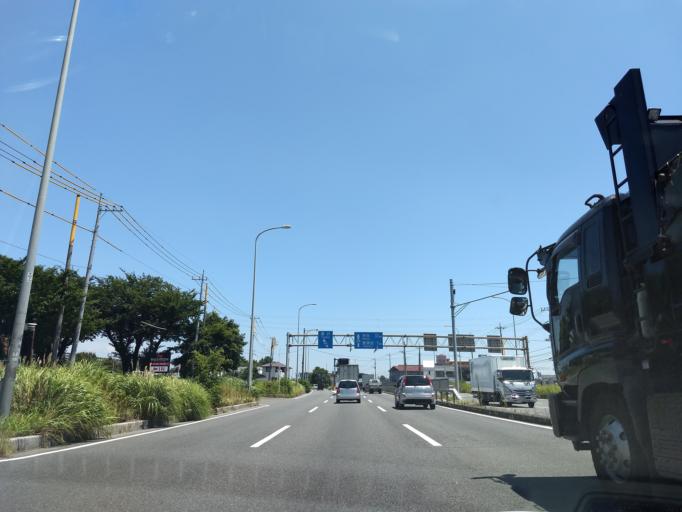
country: JP
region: Kanagawa
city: Minami-rinkan
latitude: 35.4845
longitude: 139.4586
